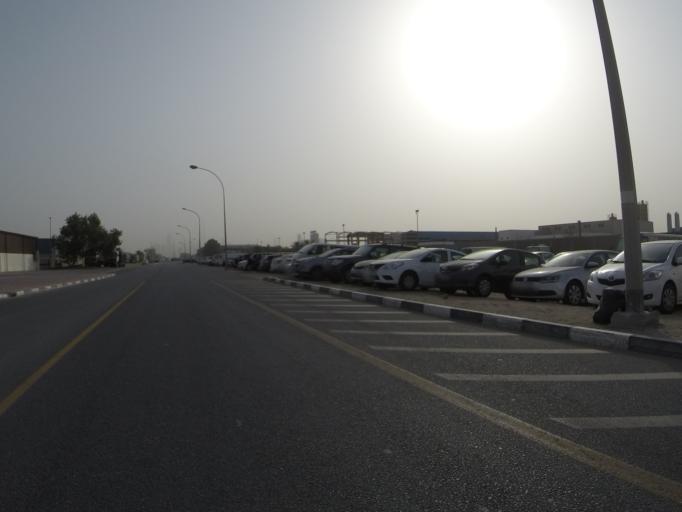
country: AE
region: Dubai
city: Dubai
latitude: 25.1447
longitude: 55.2254
